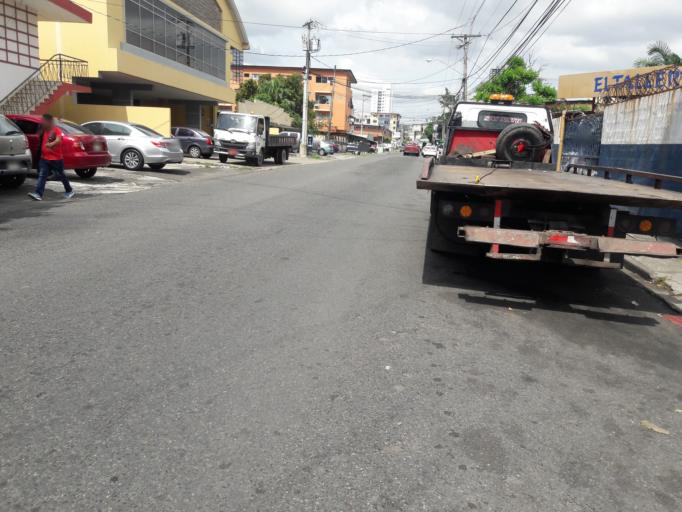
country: PA
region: Panama
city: Panama
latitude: 9.0064
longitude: -79.5027
